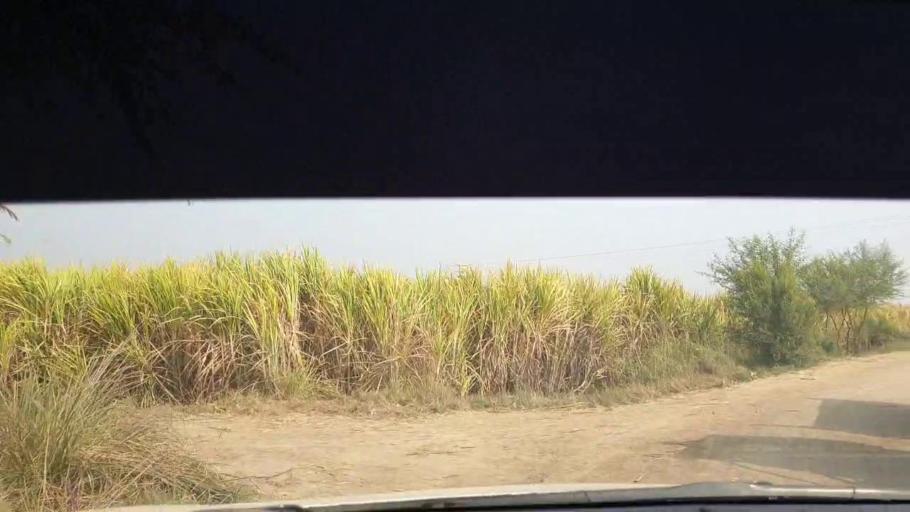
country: PK
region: Sindh
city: Berani
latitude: 25.8075
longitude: 68.8363
